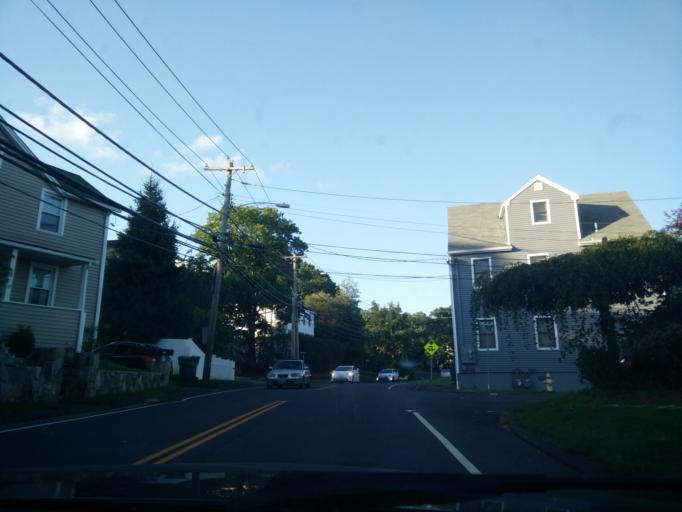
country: US
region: Connecticut
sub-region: Fairfield County
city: Bridgeport
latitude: 41.1677
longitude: -73.2361
